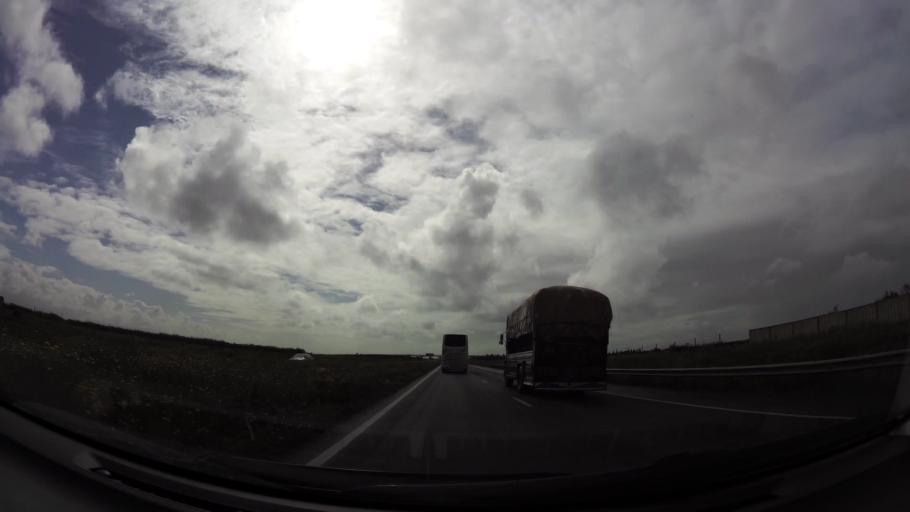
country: MA
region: Grand Casablanca
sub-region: Nouaceur
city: Dar Bouazza
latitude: 33.3536
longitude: -7.9699
